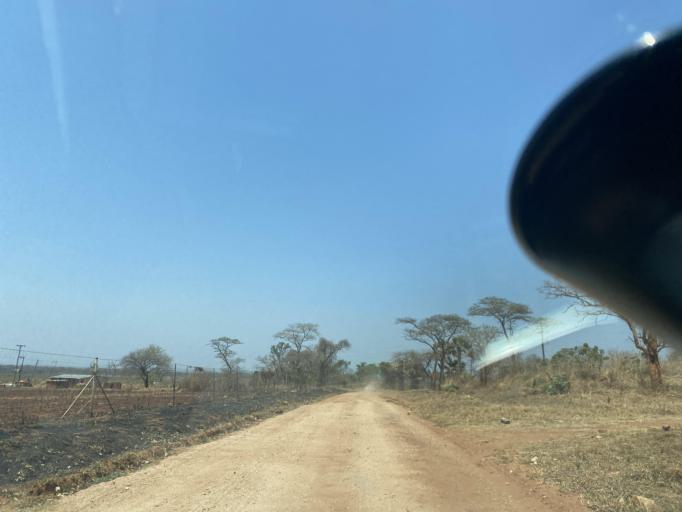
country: ZM
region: Lusaka
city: Kafue
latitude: -15.5478
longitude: 28.0689
